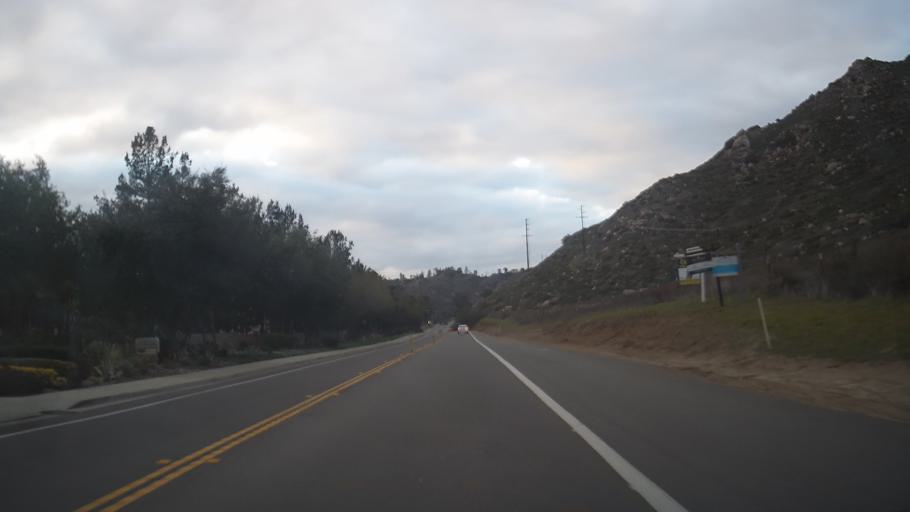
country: US
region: California
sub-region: San Diego County
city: Crest
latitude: 32.7833
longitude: -116.8782
